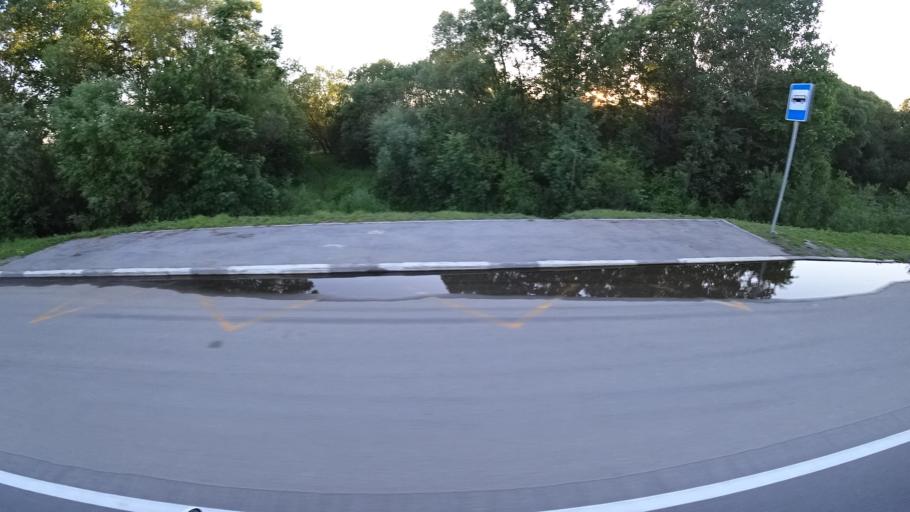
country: RU
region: Khabarovsk Krai
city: Khor
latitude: 47.8560
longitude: 134.9620
